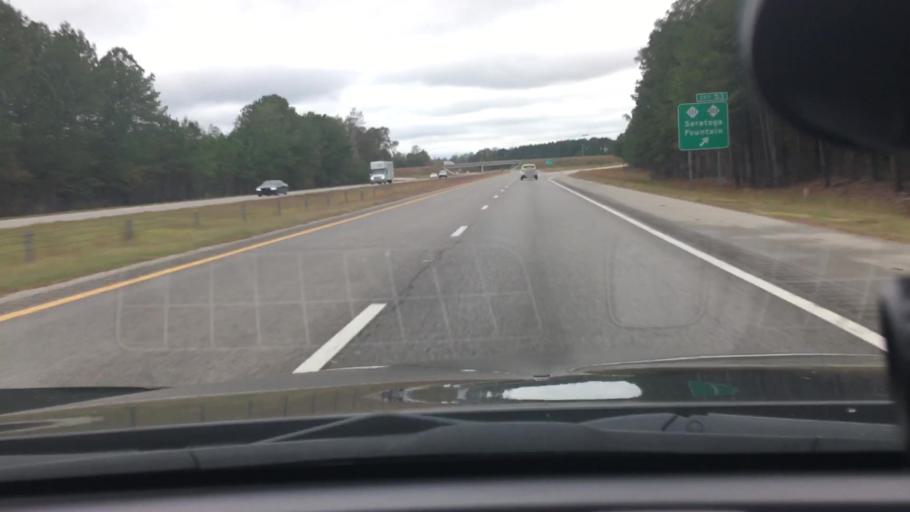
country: US
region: North Carolina
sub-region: Wilson County
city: Wilson
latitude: 35.6644
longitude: -77.7586
